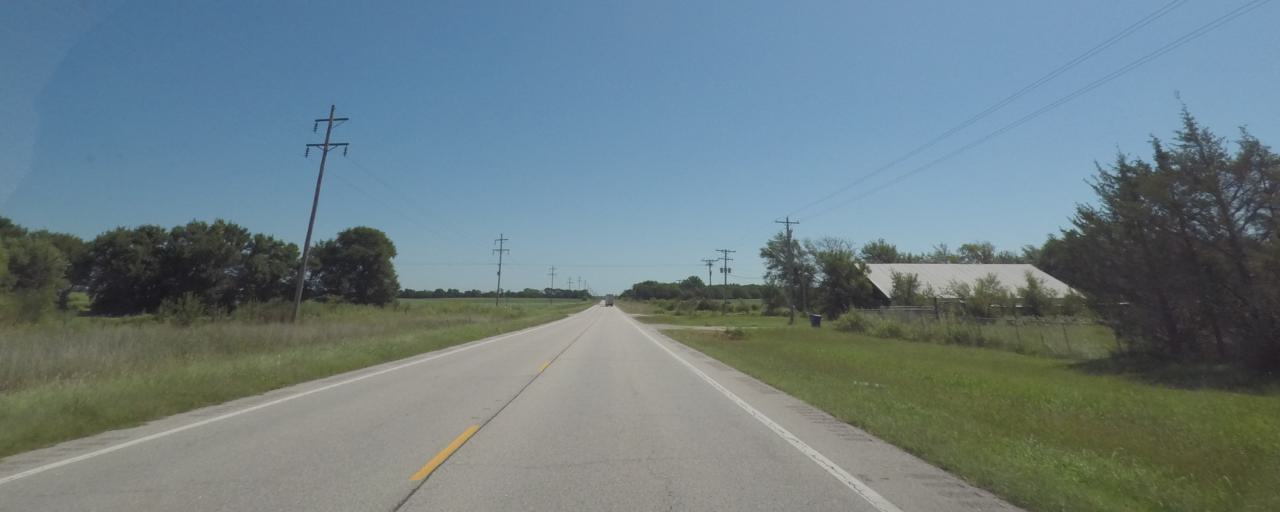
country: US
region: Kansas
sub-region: Sumner County
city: Belle Plaine
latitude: 37.3913
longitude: -97.3684
